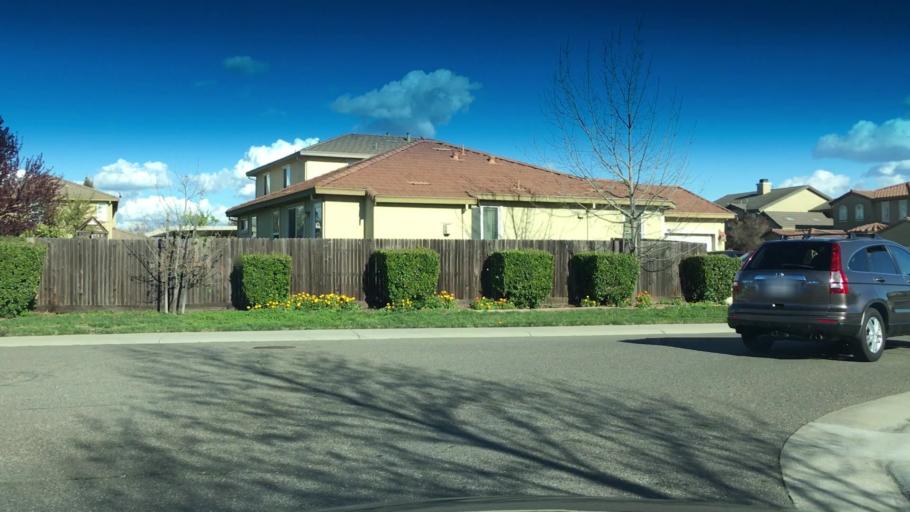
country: US
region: California
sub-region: Sacramento County
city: Laguna
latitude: 38.4443
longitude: -121.3989
